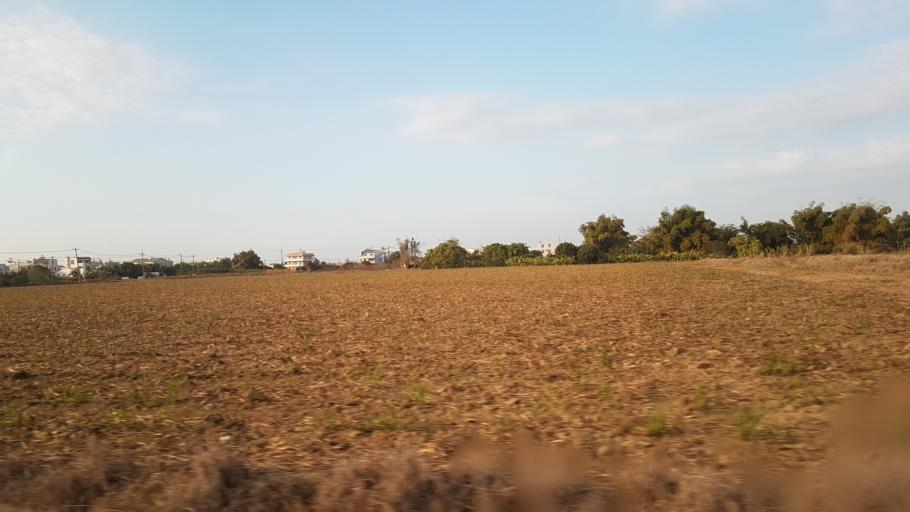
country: TW
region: Taiwan
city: Xinying
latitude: 23.3473
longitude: 120.3672
